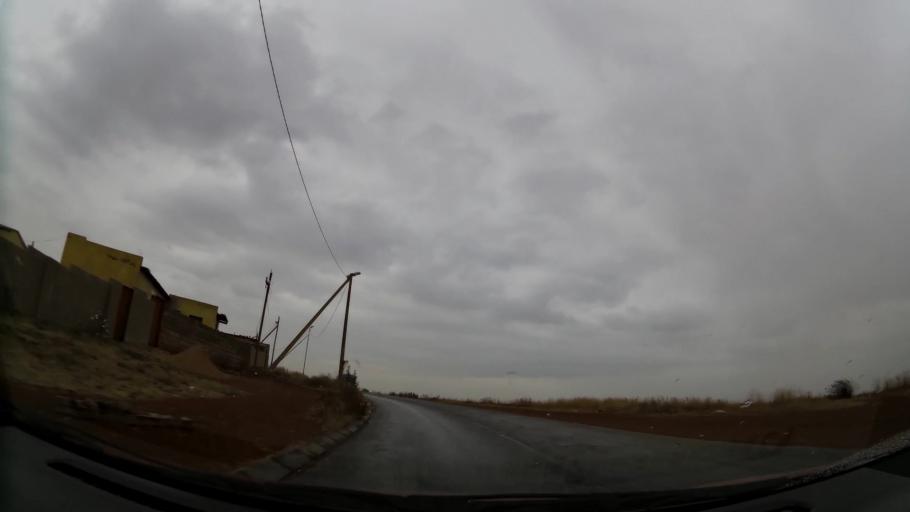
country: ZA
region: Gauteng
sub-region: West Rand District Municipality
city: Randfontein
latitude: -26.1759
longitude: 27.7790
